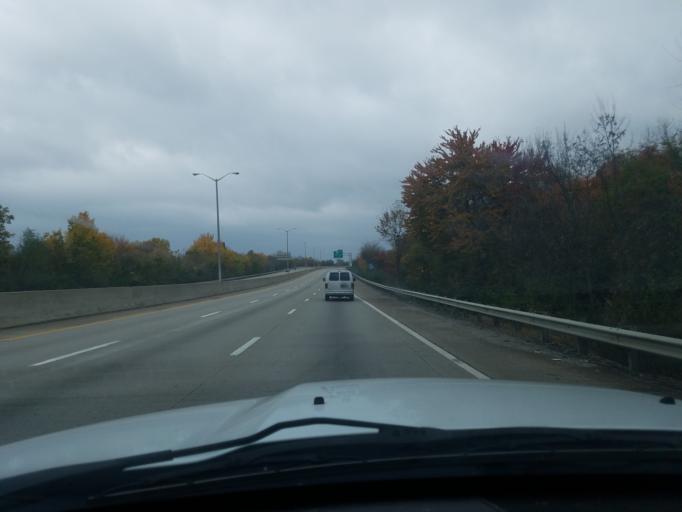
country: US
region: Kentucky
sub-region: Jefferson County
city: Shively
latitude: 38.2181
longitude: -85.8226
